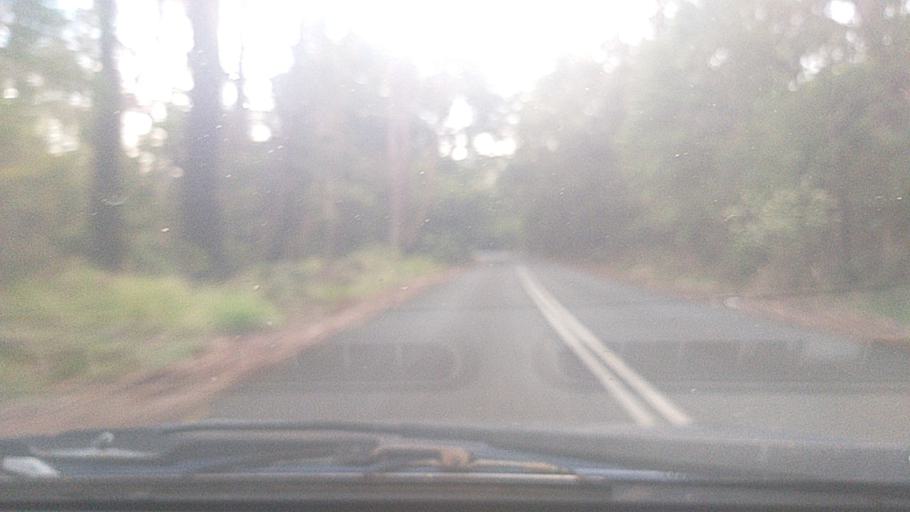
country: AU
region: New South Wales
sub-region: Wollongong
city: Mount Ousley
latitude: -34.3778
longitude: 150.8581
